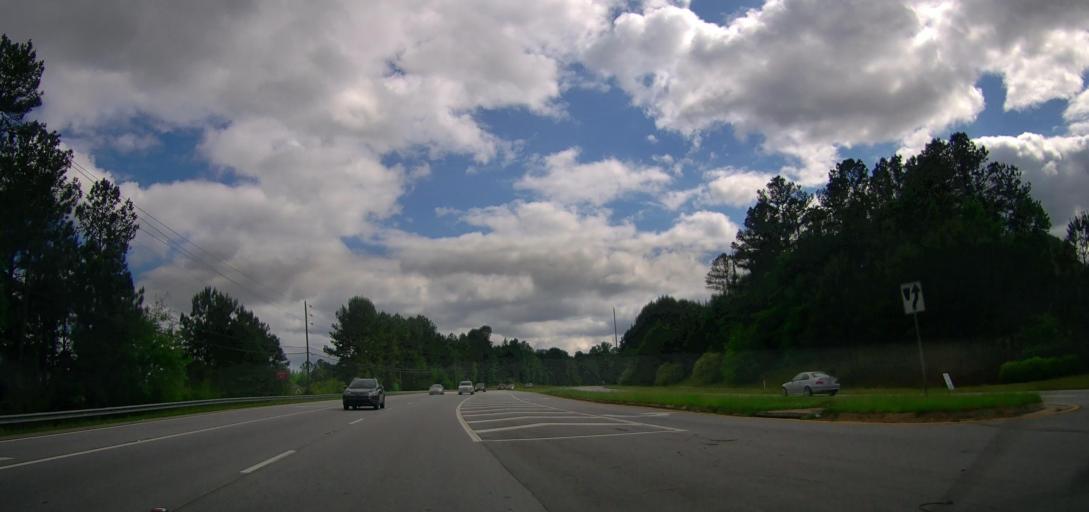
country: US
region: Georgia
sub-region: Rockdale County
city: Conyers
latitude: 33.6847
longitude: -83.9624
